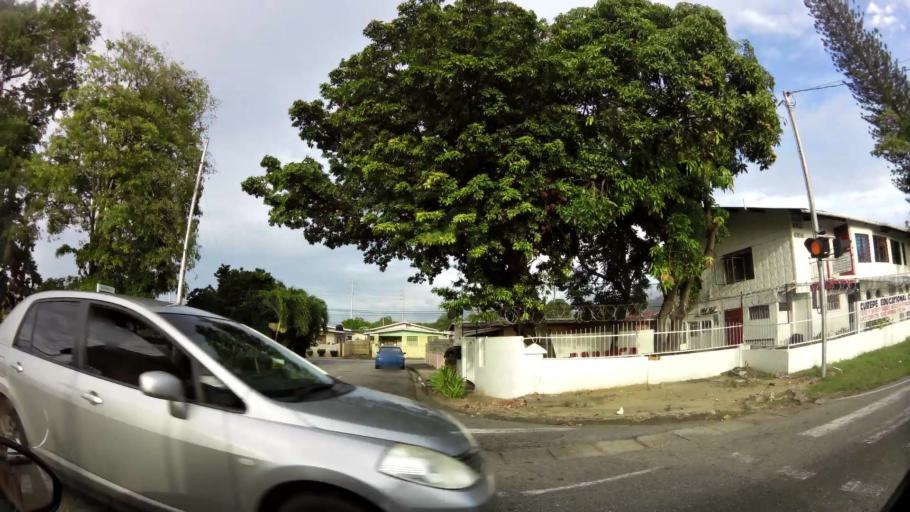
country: TT
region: Tunapuna/Piarco
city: Tunapuna
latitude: 10.6415
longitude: -61.4104
